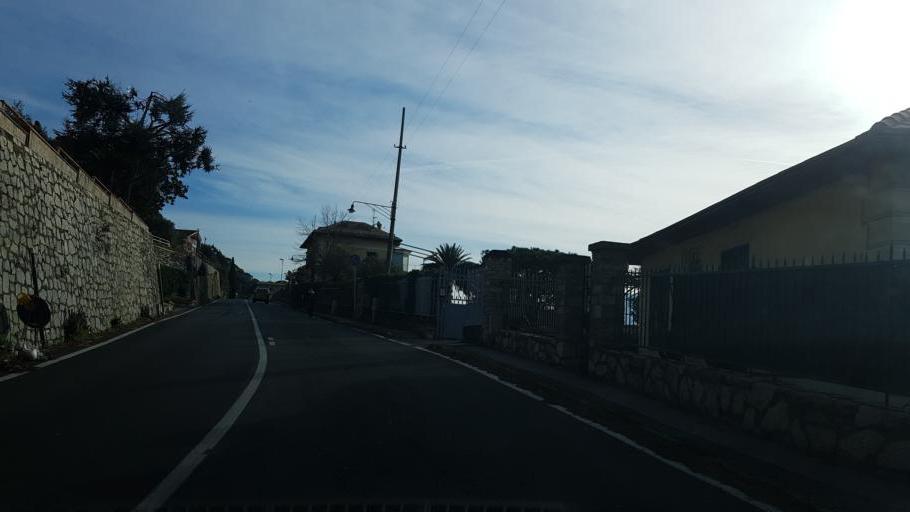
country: IT
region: Liguria
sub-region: Provincia di Genova
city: Sori
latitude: 44.3686
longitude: 9.1105
